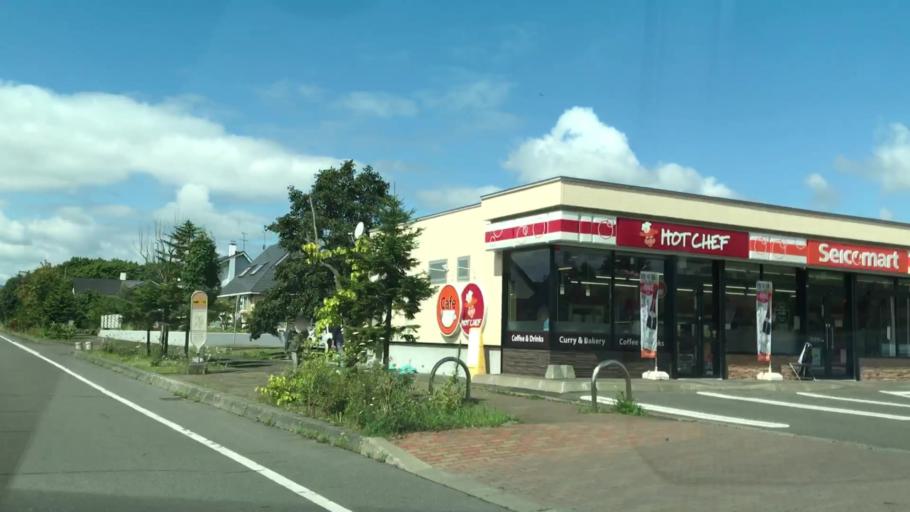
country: JP
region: Hokkaido
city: Chitose
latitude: 42.7792
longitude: 141.5997
